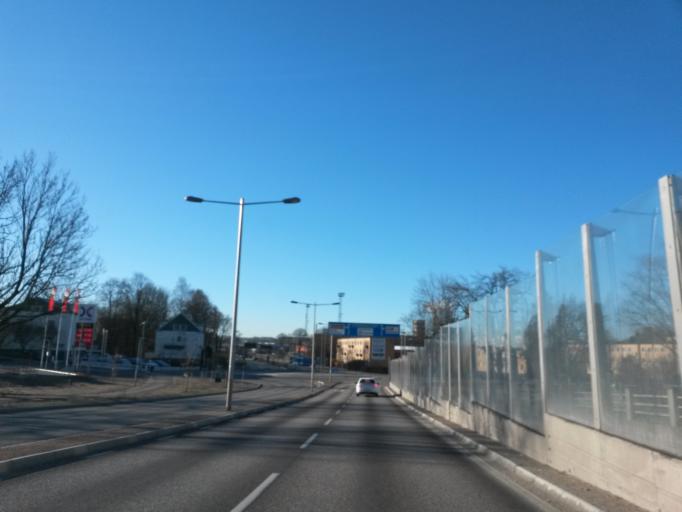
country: SE
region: Vaestra Goetaland
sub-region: Boras Kommun
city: Boras
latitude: 57.7394
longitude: 12.9378
